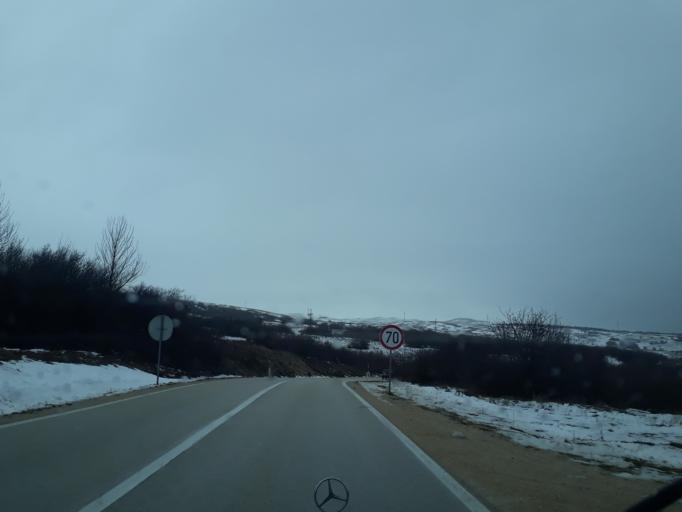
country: BA
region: Federation of Bosnia and Herzegovina
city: Tomislavgrad
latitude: 43.7979
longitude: 17.2119
